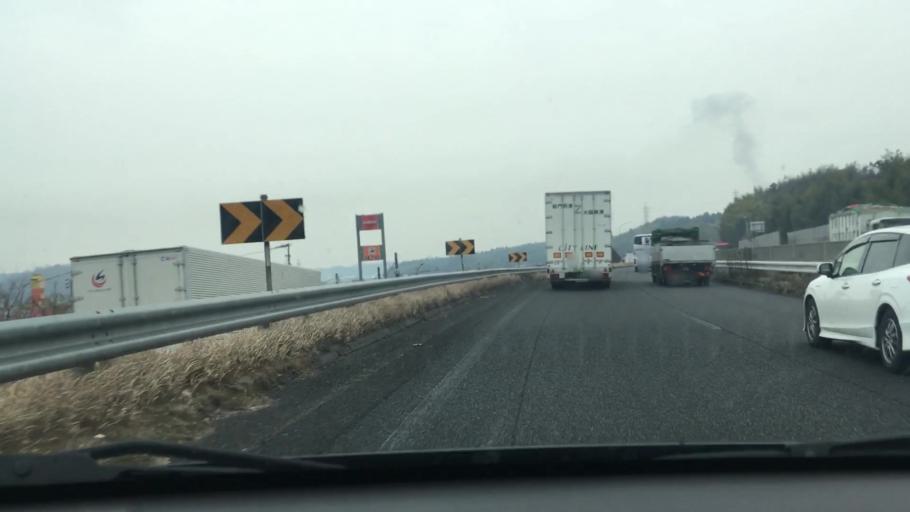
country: JP
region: Mie
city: Ueno-ebisumachi
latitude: 34.7913
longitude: 136.1626
